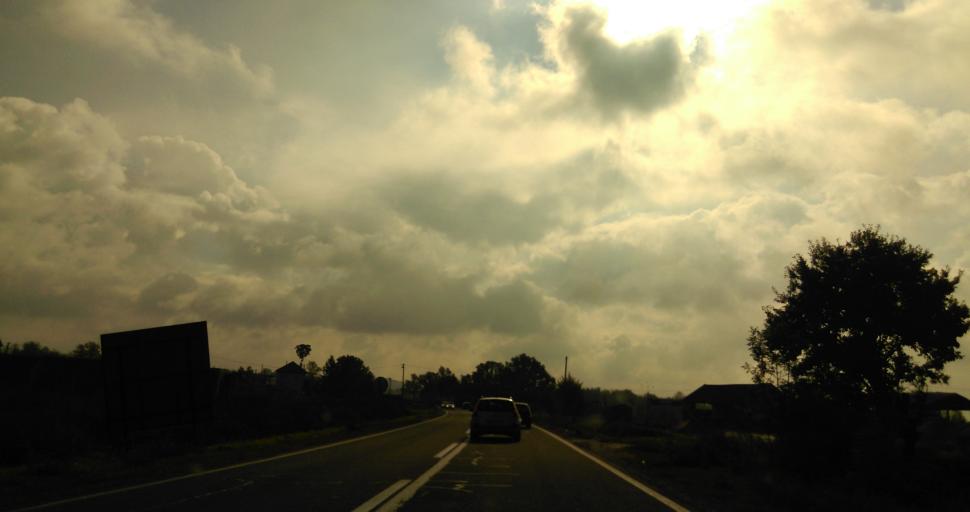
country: RS
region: Central Serbia
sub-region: Belgrade
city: Lazarevac
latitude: 44.3100
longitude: 20.2446
